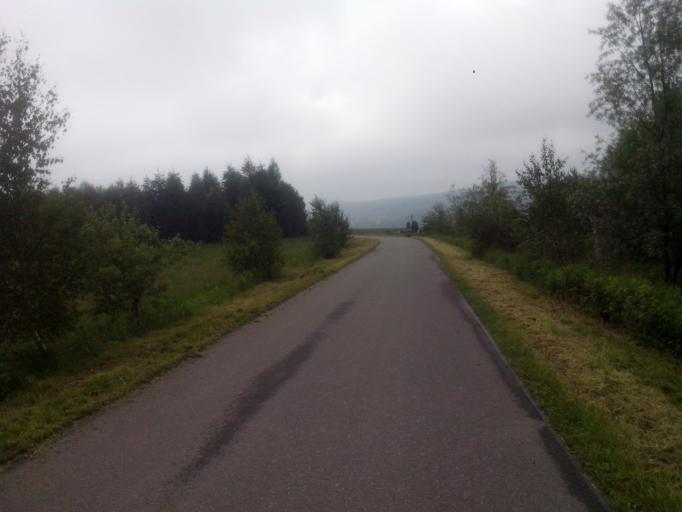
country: PL
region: Subcarpathian Voivodeship
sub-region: Powiat strzyzowski
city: Wysoka Strzyzowska
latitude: 49.8053
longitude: 21.7818
